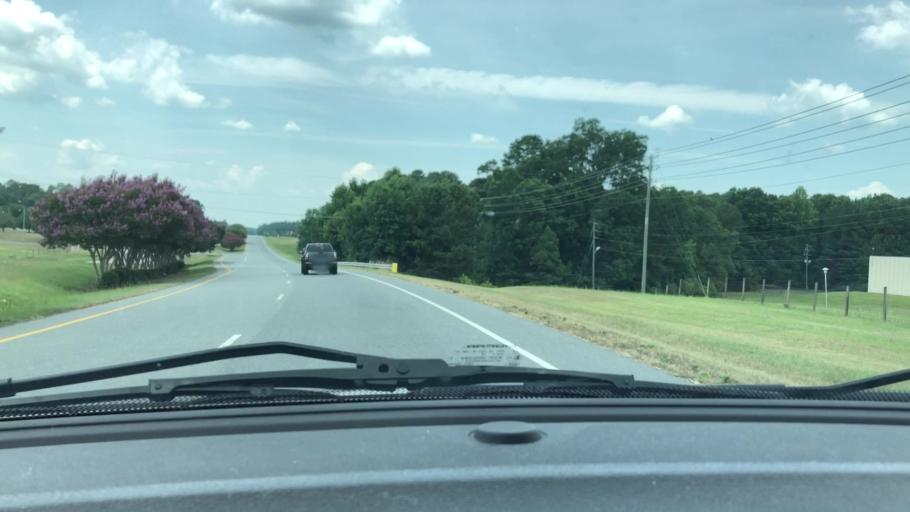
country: US
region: North Carolina
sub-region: Lee County
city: Sanford
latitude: 35.5167
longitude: -79.2167
